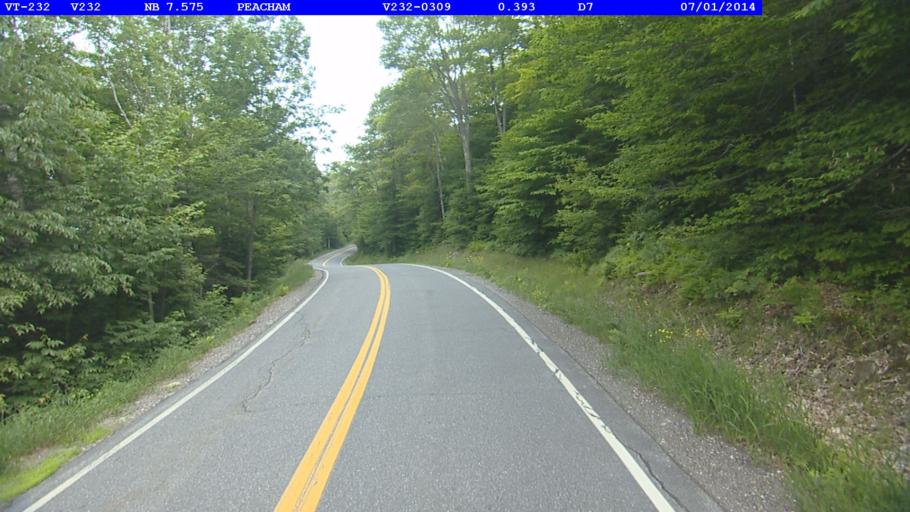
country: US
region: Vermont
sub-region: Caledonia County
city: Hardwick
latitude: 44.3015
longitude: -72.3010
